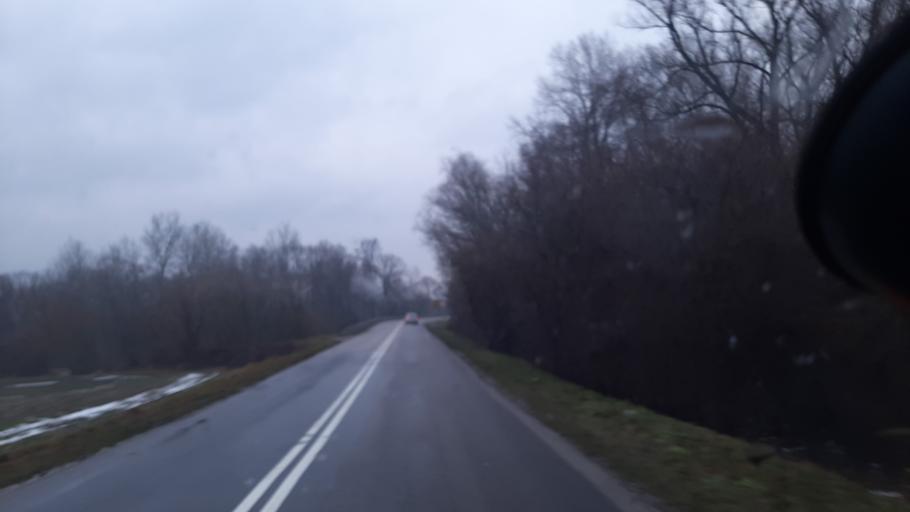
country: PL
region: Lublin Voivodeship
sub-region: Powiat lubartowski
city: Serniki
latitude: 51.4343
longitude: 22.6540
